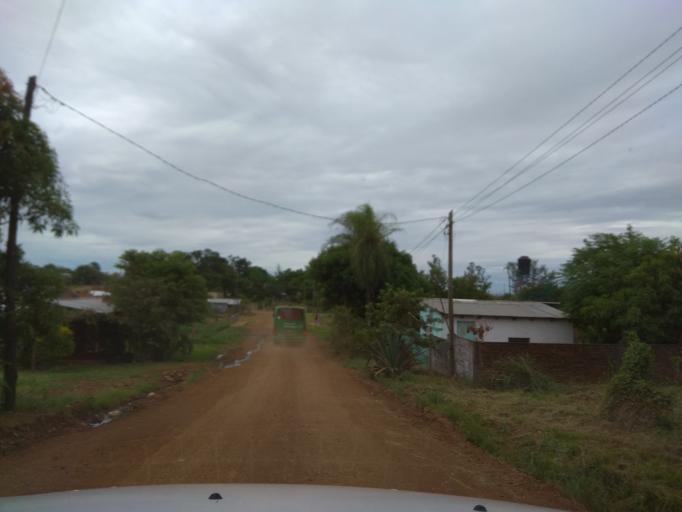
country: AR
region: Misiones
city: Garupa
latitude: -27.4376
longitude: -55.8624
